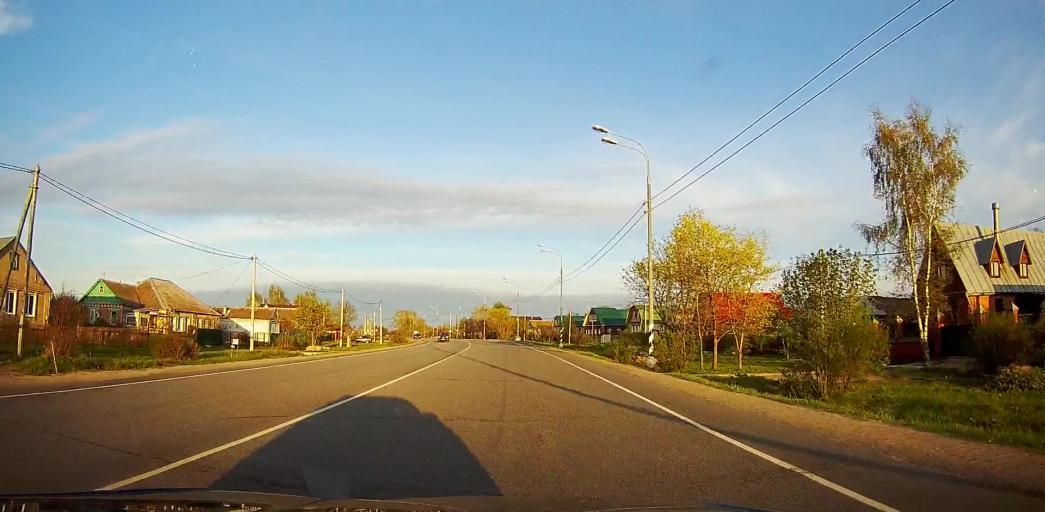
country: RU
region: Moskovskaya
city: Troitskoye
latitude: 55.2258
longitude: 38.5613
